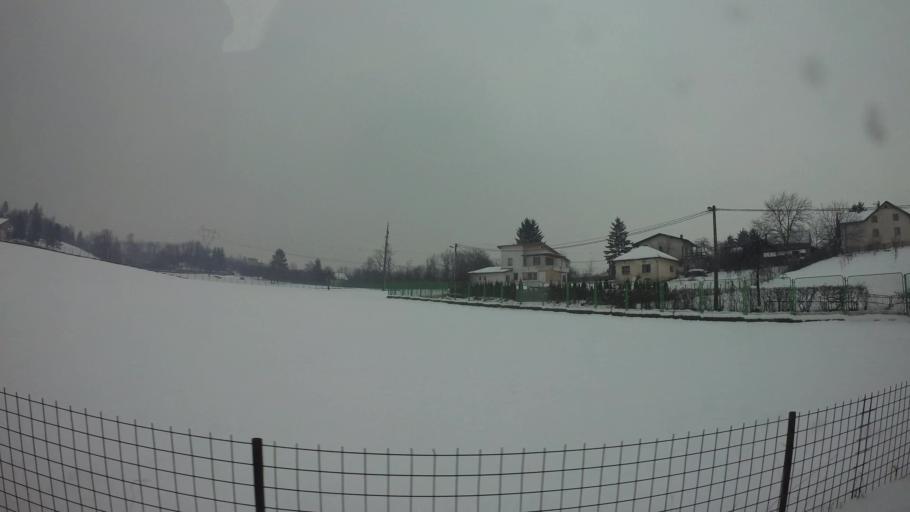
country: BA
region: Federation of Bosnia and Herzegovina
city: Hadzici
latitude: 43.8426
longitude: 18.2655
